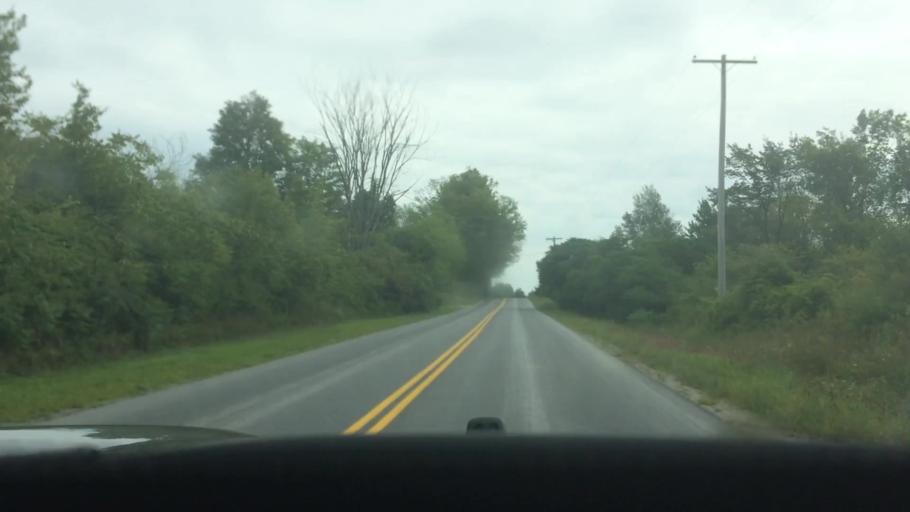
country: US
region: New York
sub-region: St. Lawrence County
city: Canton
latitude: 44.4958
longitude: -75.3046
